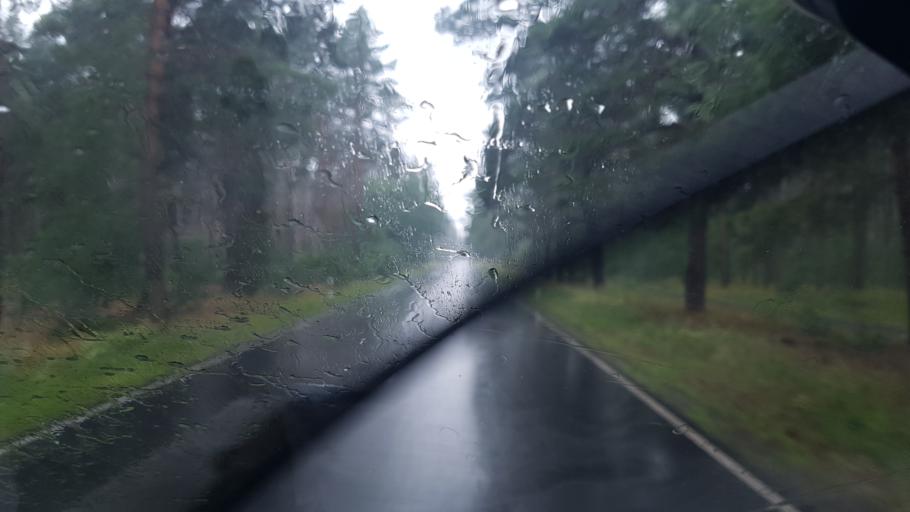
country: DE
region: Brandenburg
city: Baruth
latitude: 52.0578
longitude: 13.5379
